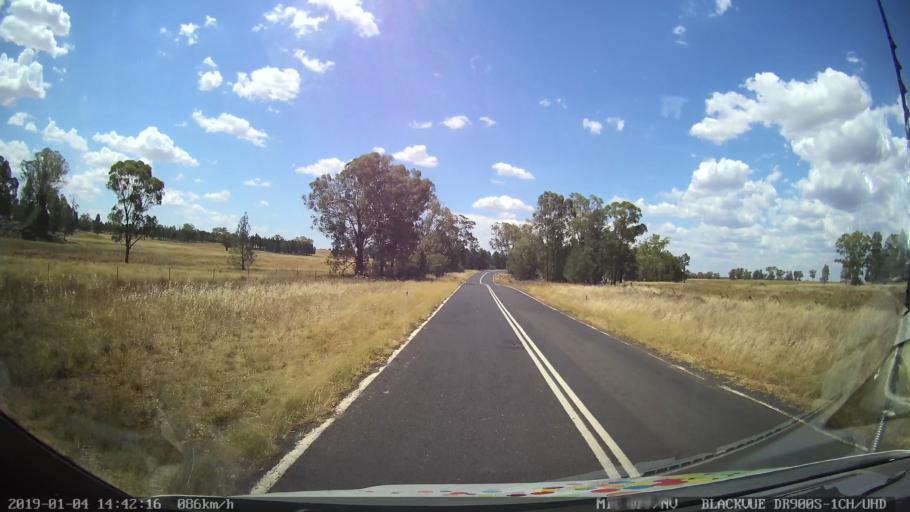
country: AU
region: New South Wales
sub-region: Dubbo Municipality
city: Dubbo
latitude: -32.1300
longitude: 148.6410
